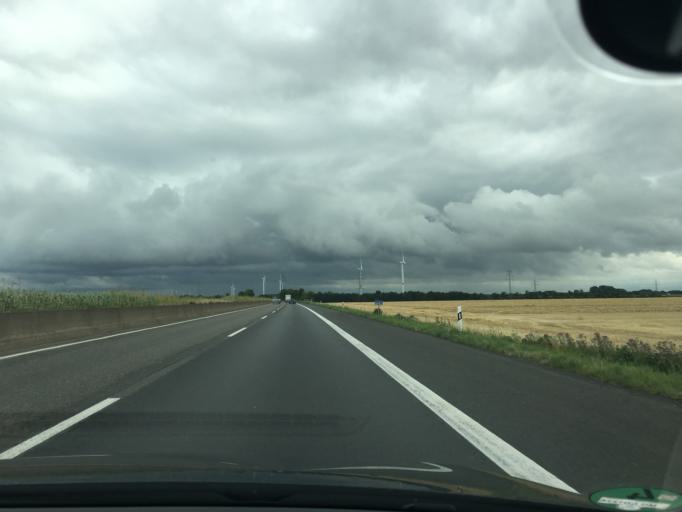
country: DE
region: North Rhine-Westphalia
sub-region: Regierungsbezirk Koln
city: Weilerswist
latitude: 50.7293
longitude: 6.7866
